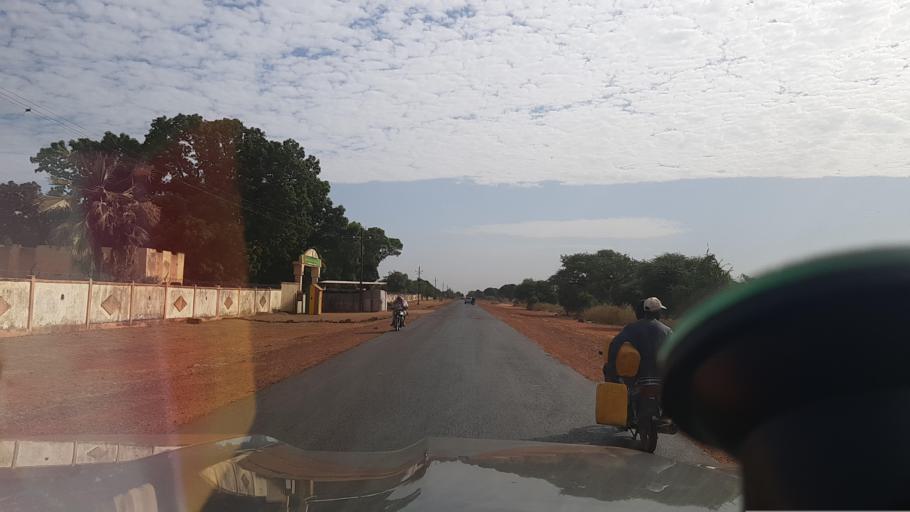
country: ML
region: Segou
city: Segou
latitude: 13.4974
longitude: -6.1621
